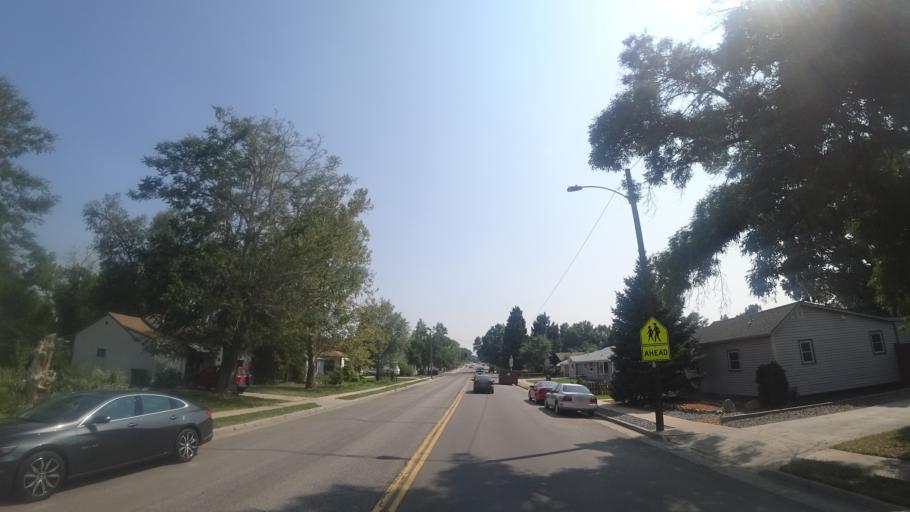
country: US
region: Colorado
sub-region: Arapahoe County
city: Englewood
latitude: 39.6287
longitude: -104.9832
